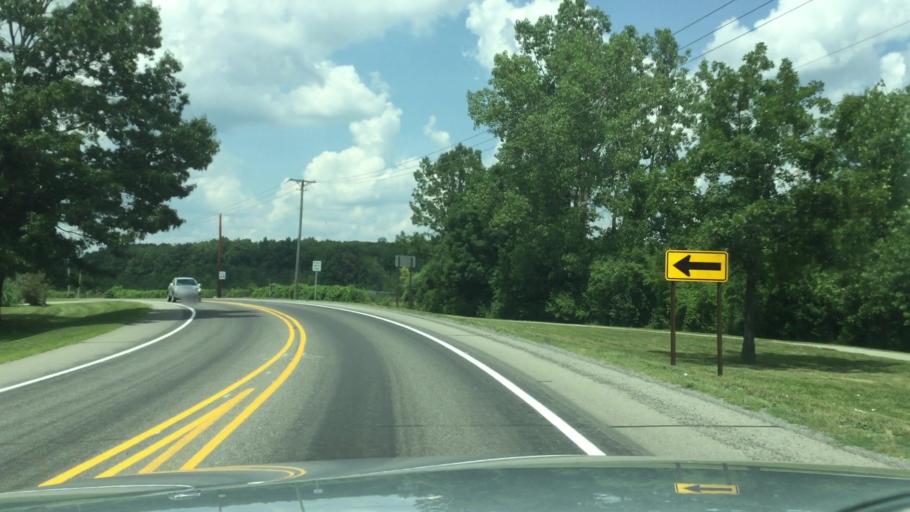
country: US
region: Michigan
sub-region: Washtenaw County
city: Ypsilanti
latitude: 42.2034
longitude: -83.6101
